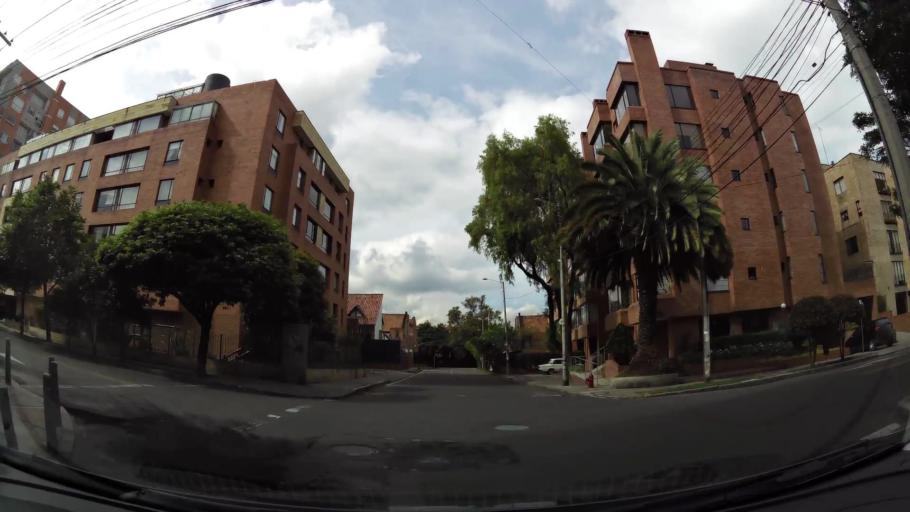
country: CO
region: Bogota D.C.
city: Barrio San Luis
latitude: 4.7218
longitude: -74.0308
